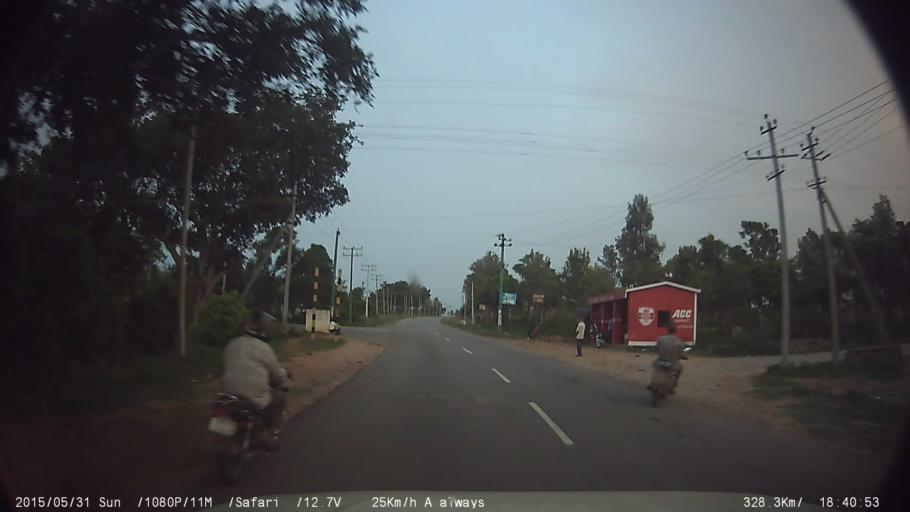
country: IN
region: Karnataka
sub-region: Mysore
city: Nanjangud
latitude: 12.1485
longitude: 76.7892
